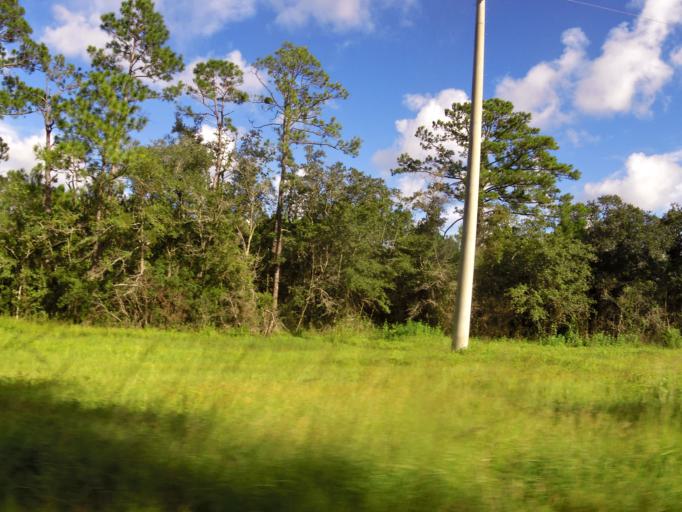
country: US
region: Georgia
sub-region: Glynn County
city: Brunswick
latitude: 31.1183
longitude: -81.6103
